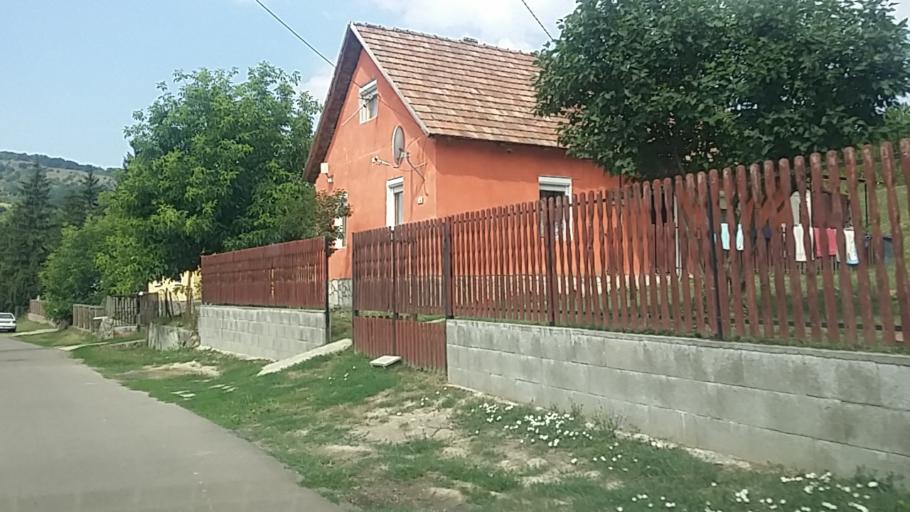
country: HU
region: Nograd
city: Matraverebely
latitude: 47.9757
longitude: 19.7721
